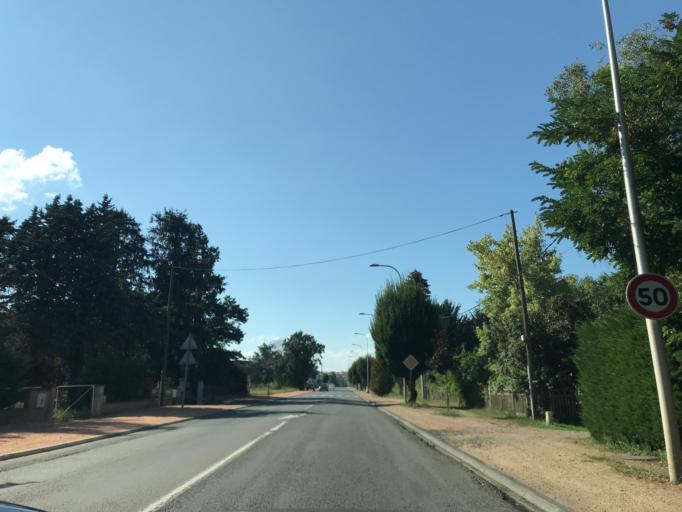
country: FR
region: Auvergne
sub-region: Departement du Puy-de-Dome
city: Pont-du-Chateau
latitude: 45.7892
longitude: 3.2654
